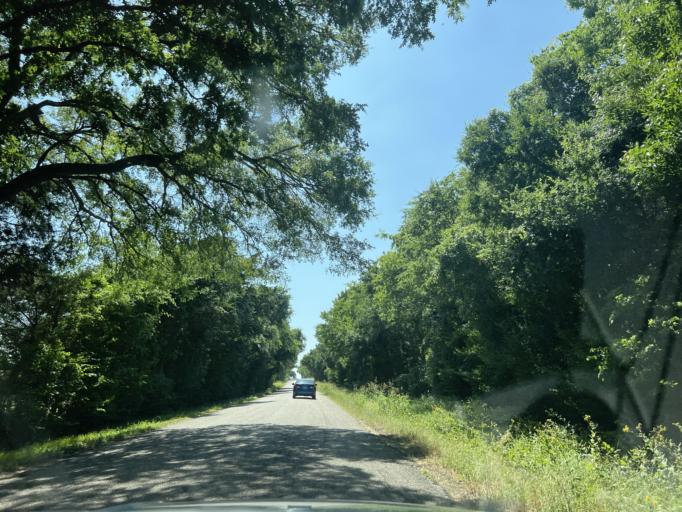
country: US
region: Texas
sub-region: Washington County
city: Brenham
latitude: 30.1567
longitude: -96.5084
